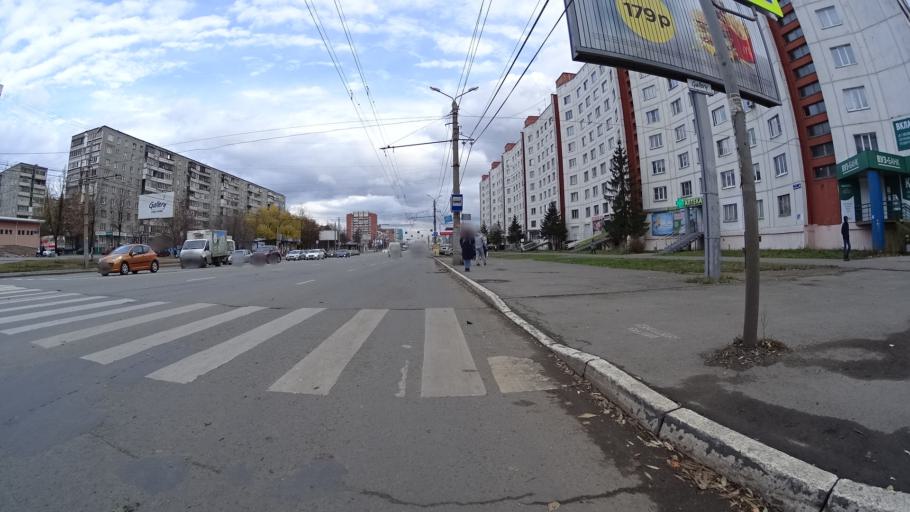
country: RU
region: Chelyabinsk
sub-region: Gorod Chelyabinsk
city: Chelyabinsk
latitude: 55.1943
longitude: 61.3144
